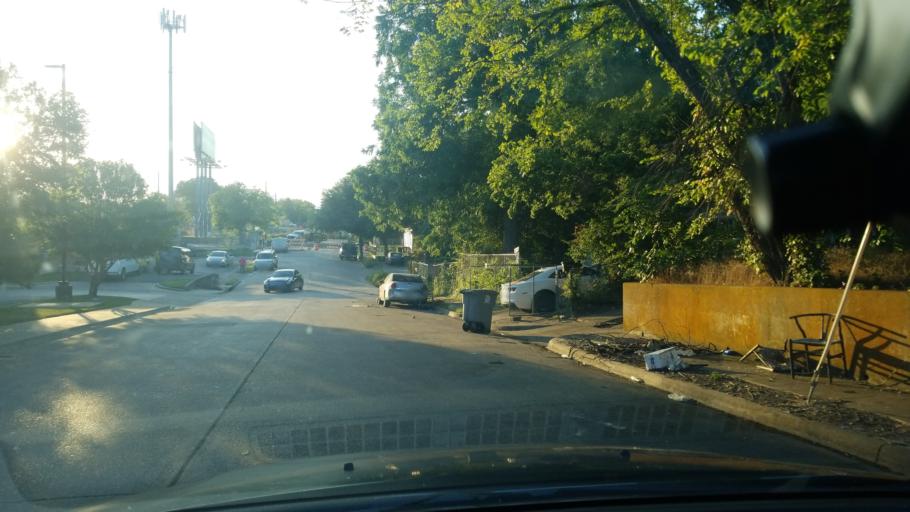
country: US
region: Texas
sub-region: Dallas County
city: Cockrell Hill
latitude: 32.7195
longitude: -96.8297
